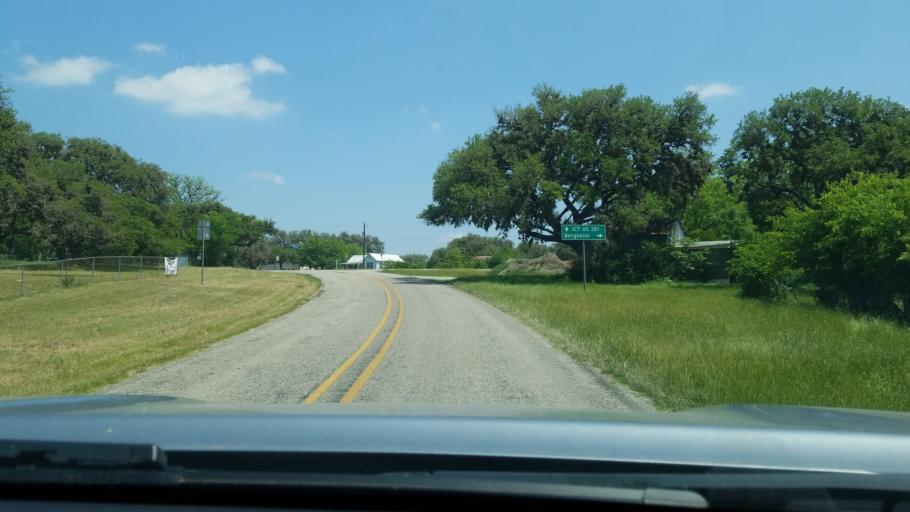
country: US
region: Texas
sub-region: Blanco County
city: Blanco
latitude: 29.9694
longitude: -98.5242
